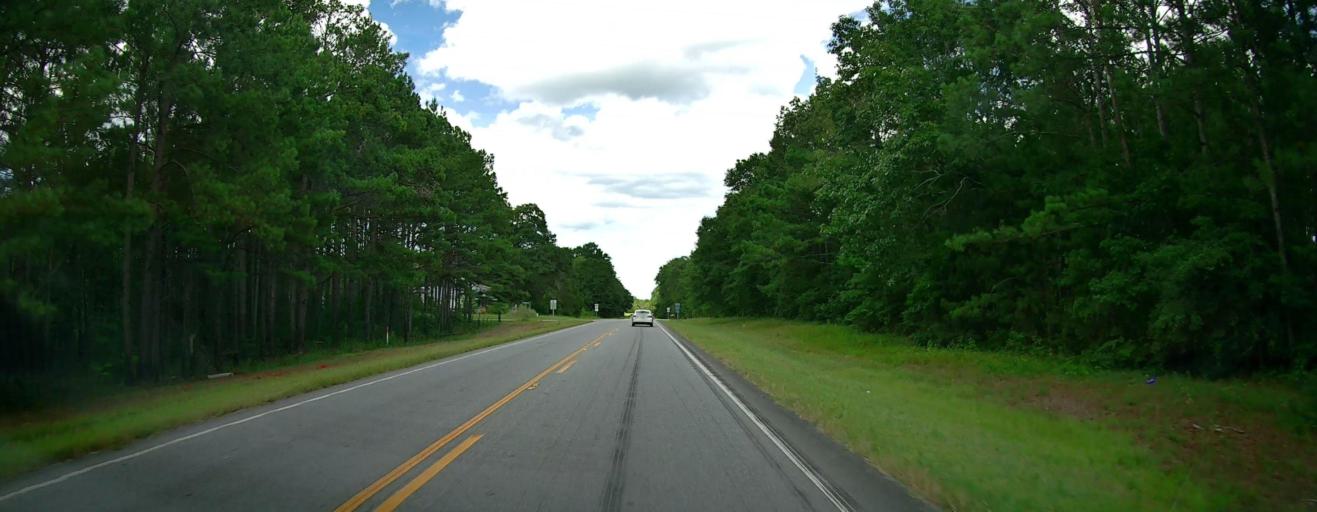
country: US
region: Alabama
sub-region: Lee County
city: Opelika
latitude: 32.4406
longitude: -85.3312
